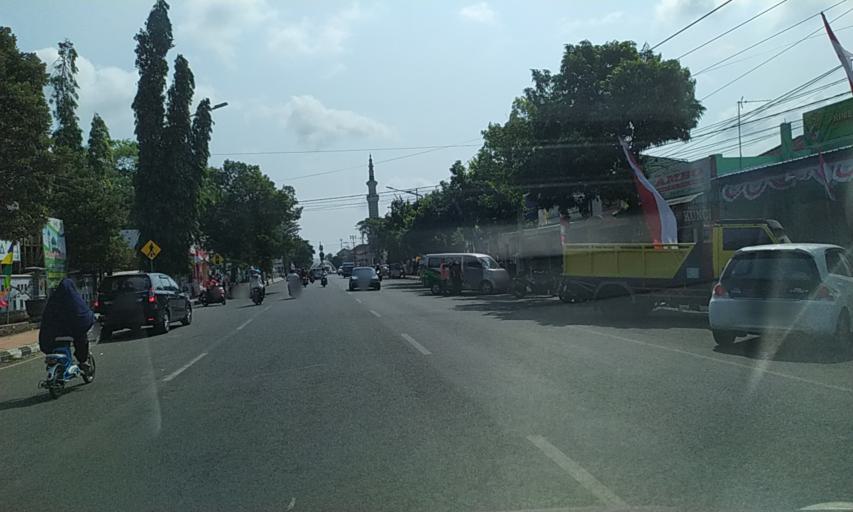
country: ID
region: Central Java
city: Karangbadar Kidul
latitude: -7.7279
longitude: 109.0110
